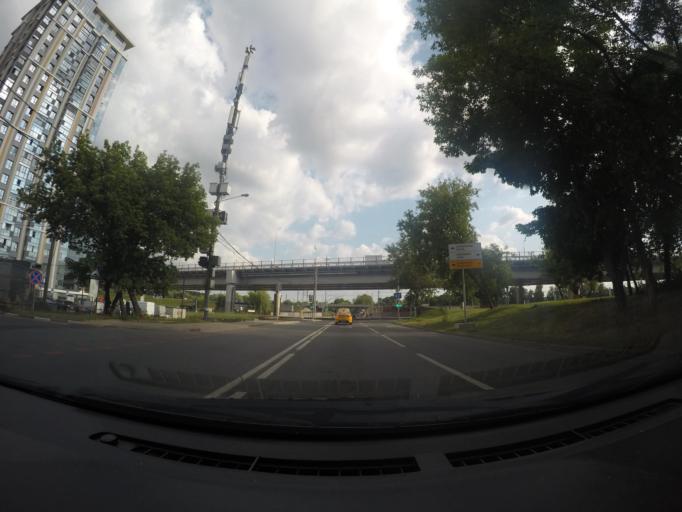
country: RU
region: Moscow
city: Sviblovo
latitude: 55.8477
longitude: 37.6264
